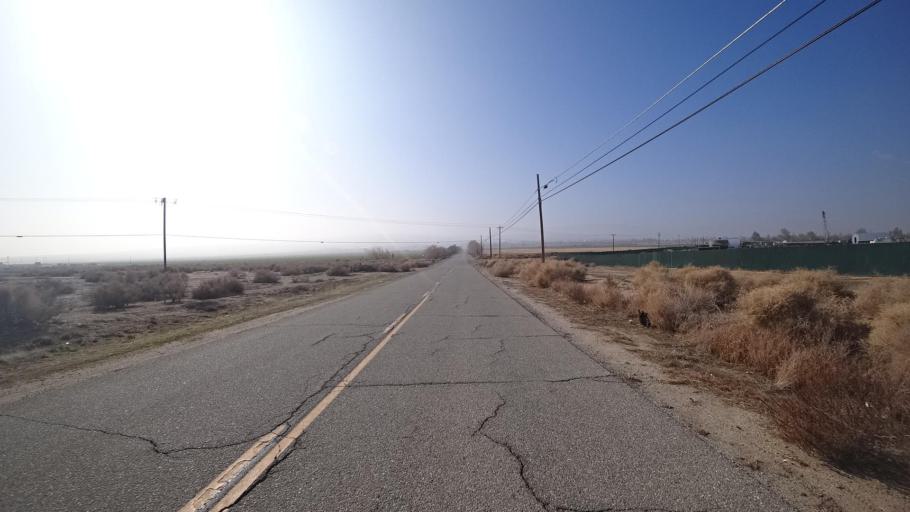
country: US
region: California
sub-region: Kern County
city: Ford City
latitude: 35.1519
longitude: -119.4315
